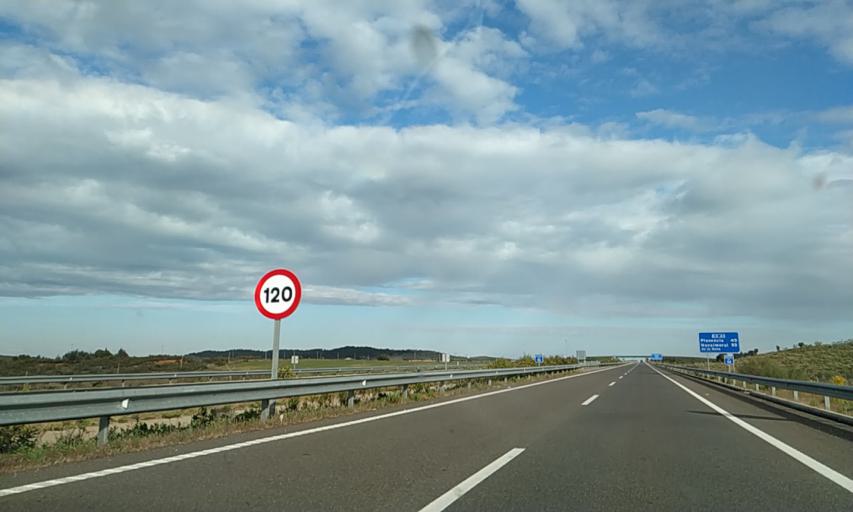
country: ES
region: Extremadura
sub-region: Provincia de Caceres
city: Casas de Don Gomez
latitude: 40.0223
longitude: -6.5976
